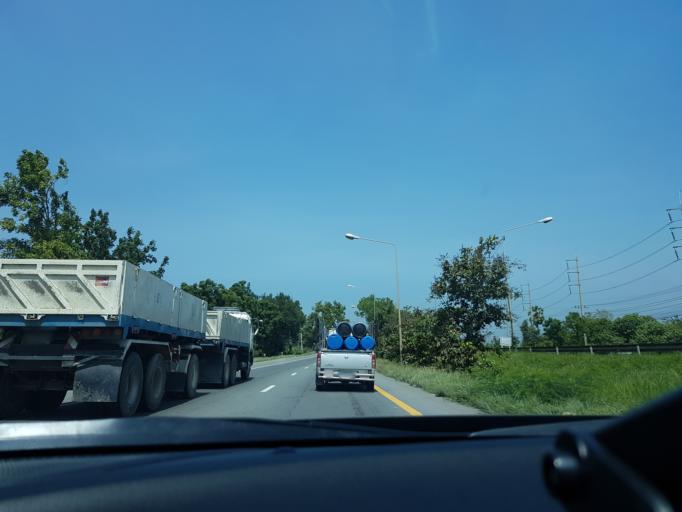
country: TH
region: Sara Buri
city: Saraburi
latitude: 14.5220
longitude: 100.8893
